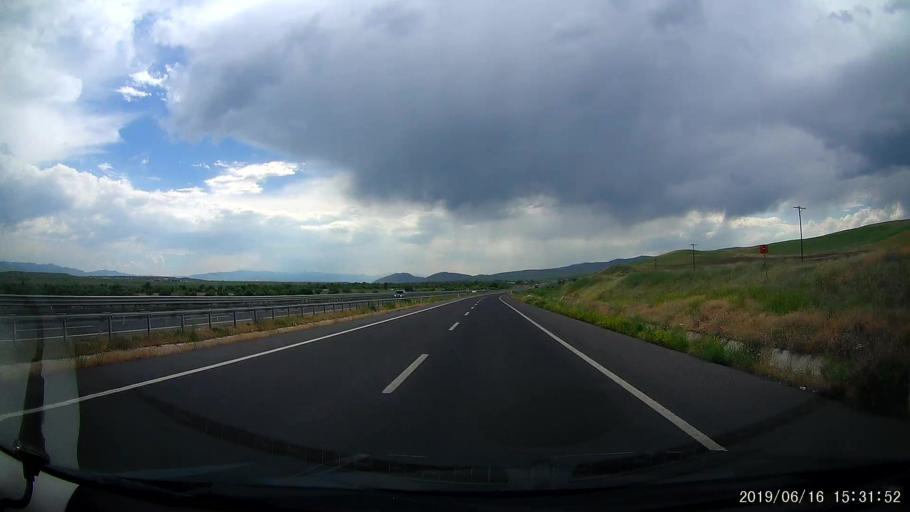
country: TR
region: Erzurum
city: Horasan
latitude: 40.0306
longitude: 42.0656
